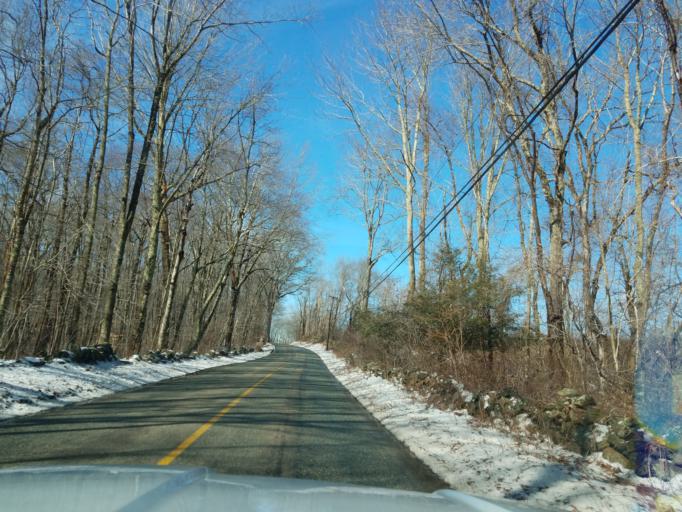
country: US
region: Connecticut
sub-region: New London County
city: Preston City
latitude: 41.4726
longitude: -71.9246
